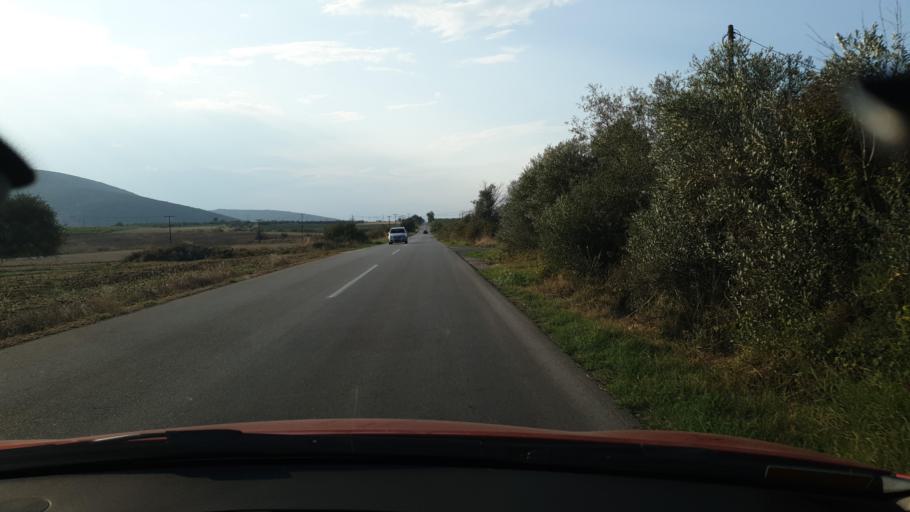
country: GR
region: Thessaly
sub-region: Nomos Magnisias
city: Sourpi
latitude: 39.1246
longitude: 22.8598
